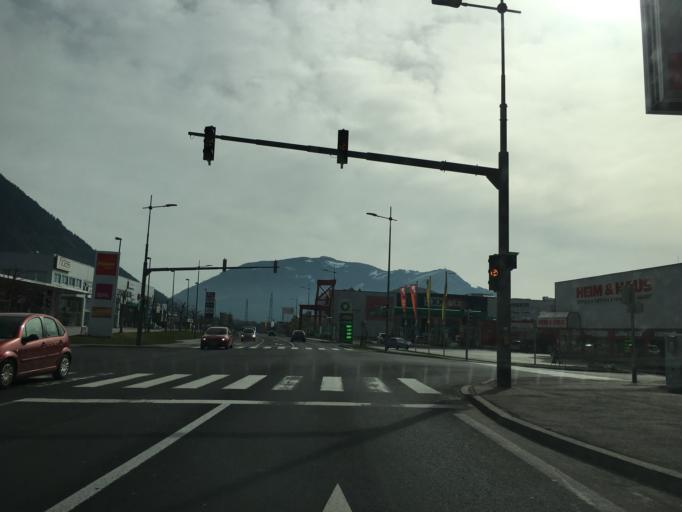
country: AT
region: Styria
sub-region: Politischer Bezirk Liezen
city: Liezen
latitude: 47.5596
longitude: 14.2520
